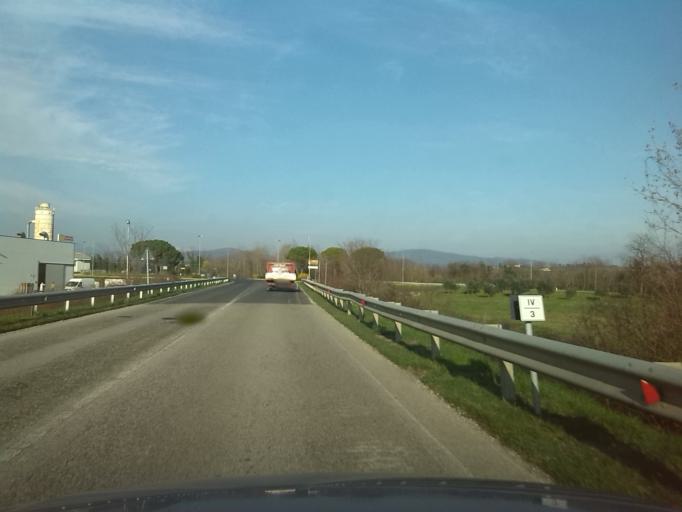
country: IT
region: Friuli Venezia Giulia
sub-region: Provincia di Udine
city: Orsaria
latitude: 46.0208
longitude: 13.3927
